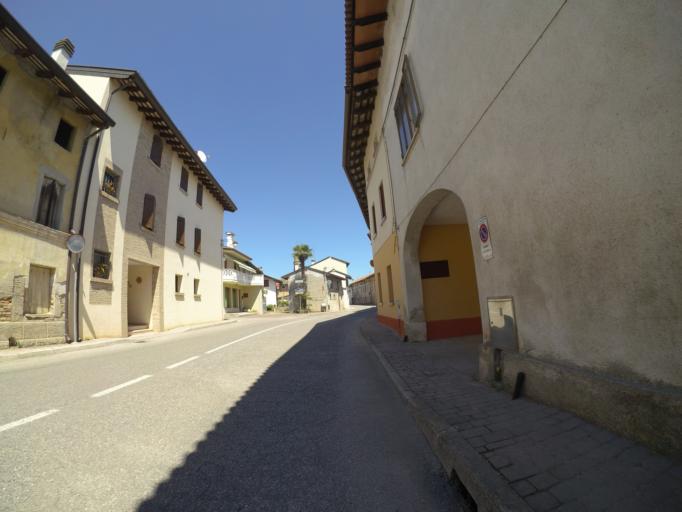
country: IT
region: Friuli Venezia Giulia
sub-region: Provincia di Udine
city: Teor
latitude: 45.8540
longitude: 13.0538
